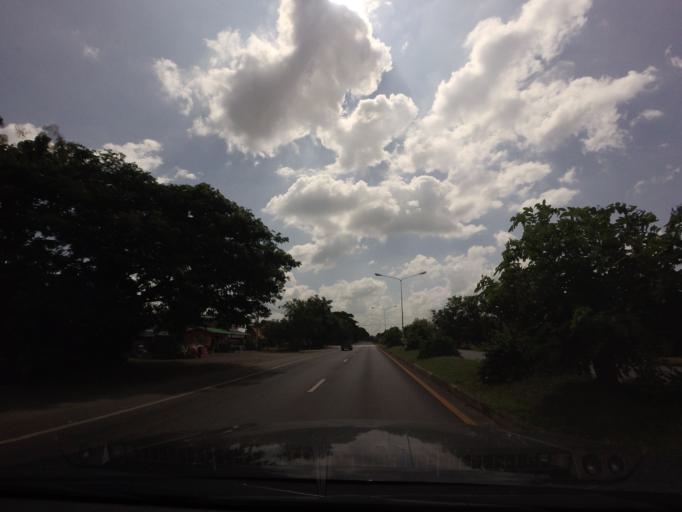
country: TH
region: Phetchabun
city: Nong Phai
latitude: 16.1316
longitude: 101.0452
